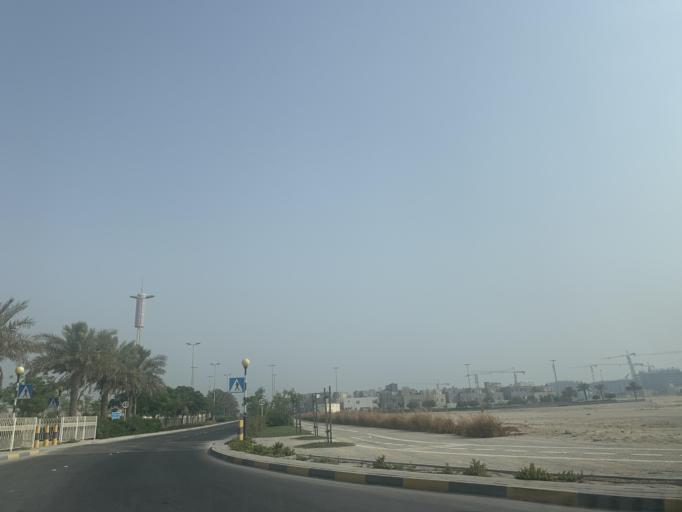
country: BH
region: Manama
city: Jidd Hafs
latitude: 26.2308
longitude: 50.4557
